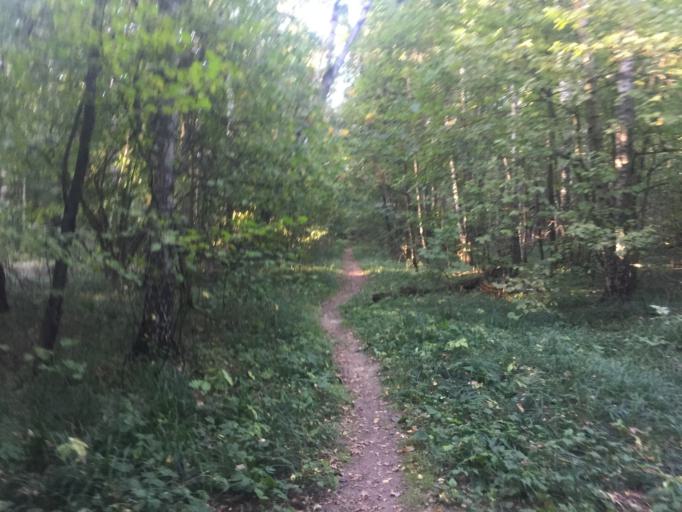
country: RU
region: Moscow
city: Gol'yanovo
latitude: 55.8431
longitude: 37.7966
